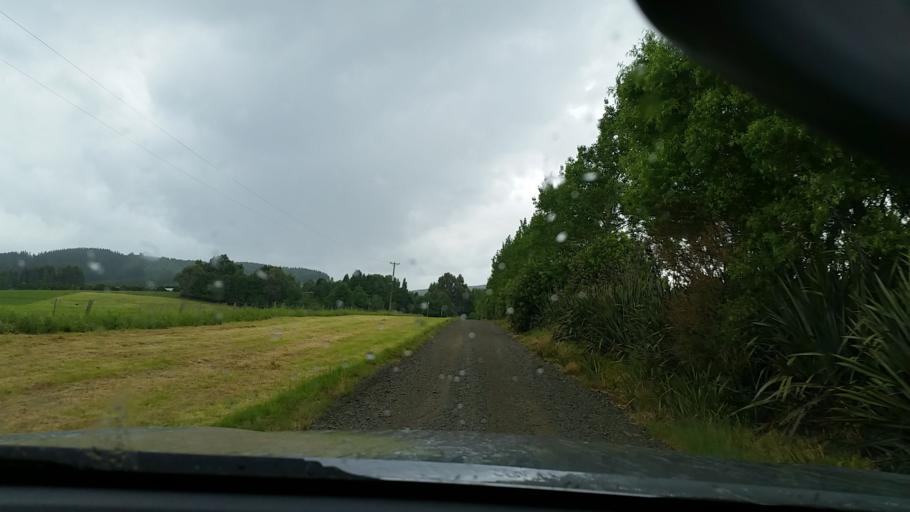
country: NZ
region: Southland
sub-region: Southland District
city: Winton
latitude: -46.0055
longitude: 168.2456
